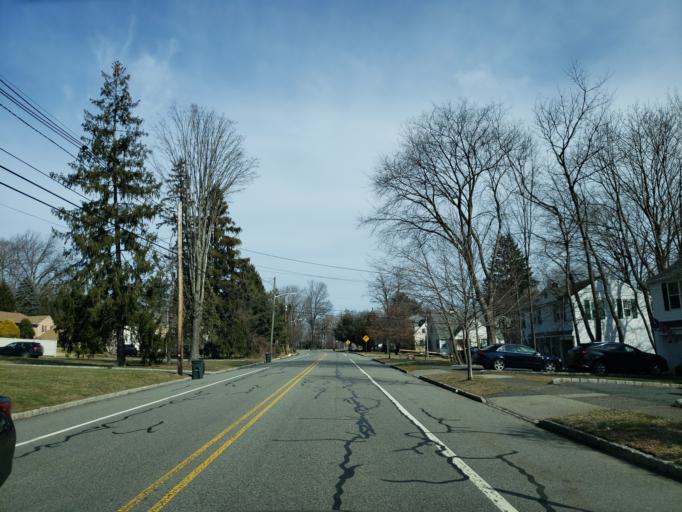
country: US
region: New Jersey
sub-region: Essex County
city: Cedar Grove
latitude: 40.8623
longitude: -74.2352
